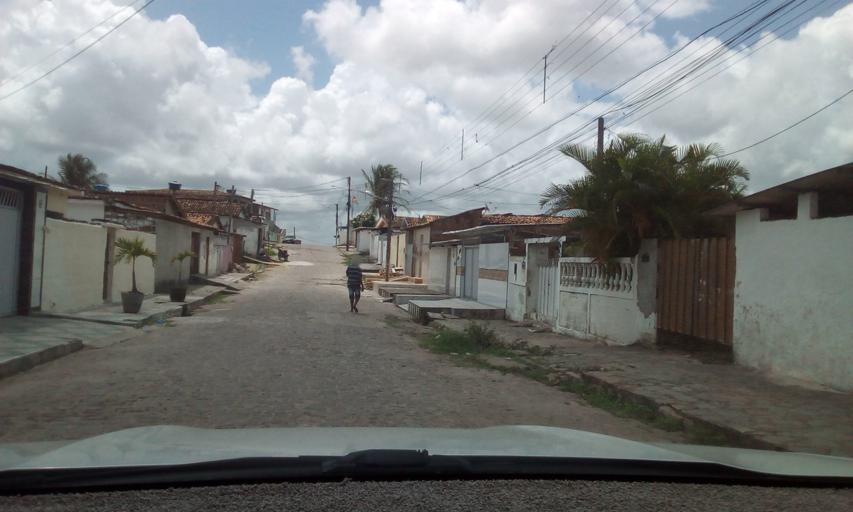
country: BR
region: Paraiba
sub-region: Joao Pessoa
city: Joao Pessoa
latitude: -7.1523
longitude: -34.8912
